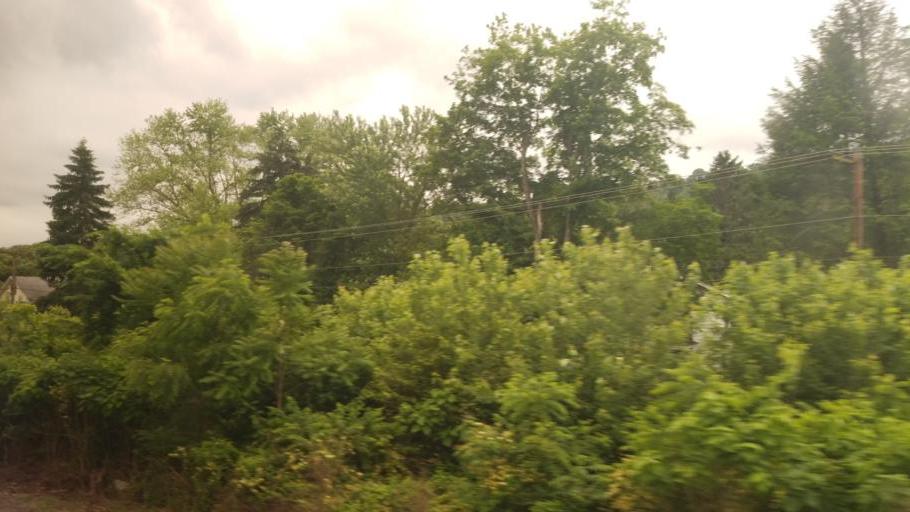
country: US
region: Maryland
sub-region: Allegany County
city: La Vale
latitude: 39.6763
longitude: -78.7887
